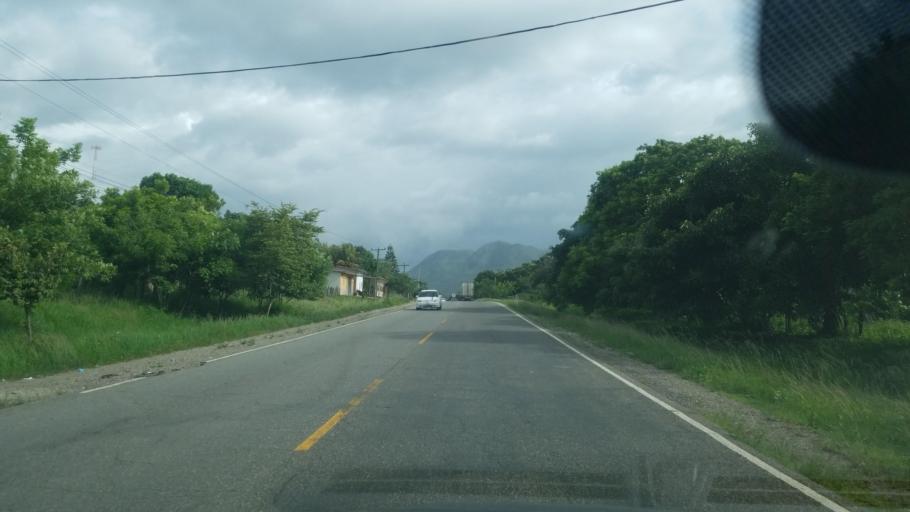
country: HN
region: Ocotepeque
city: Antigua Ocotepeque
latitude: 14.3821
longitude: -89.2080
